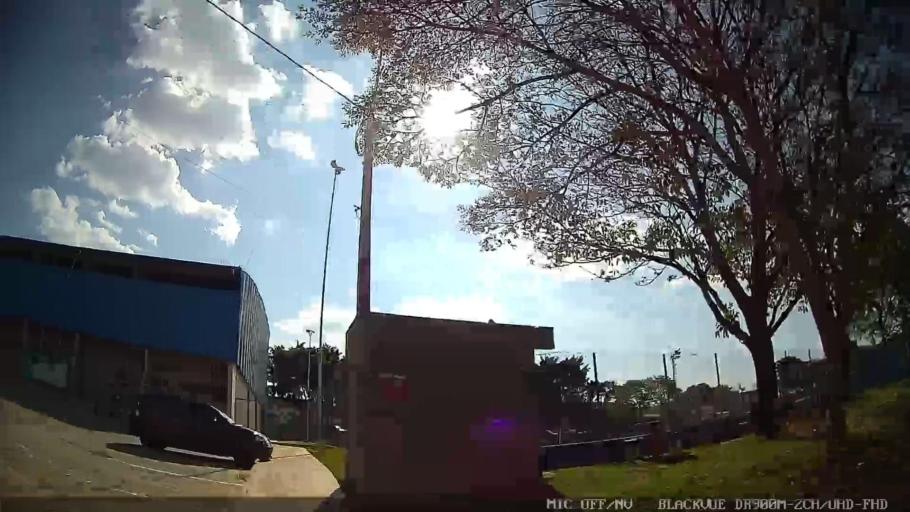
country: BR
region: Sao Paulo
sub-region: Cabreuva
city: Cabreuva
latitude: -23.2509
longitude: -47.0529
